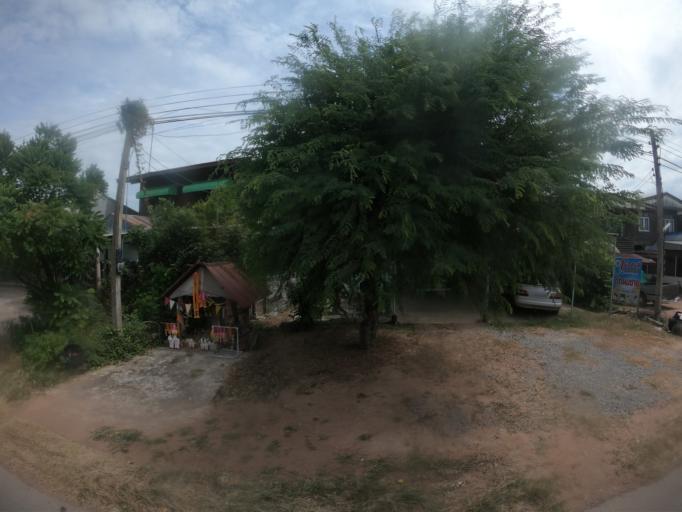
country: TH
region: Maha Sarakham
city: Chiang Yuen
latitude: 16.3950
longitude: 103.1001
